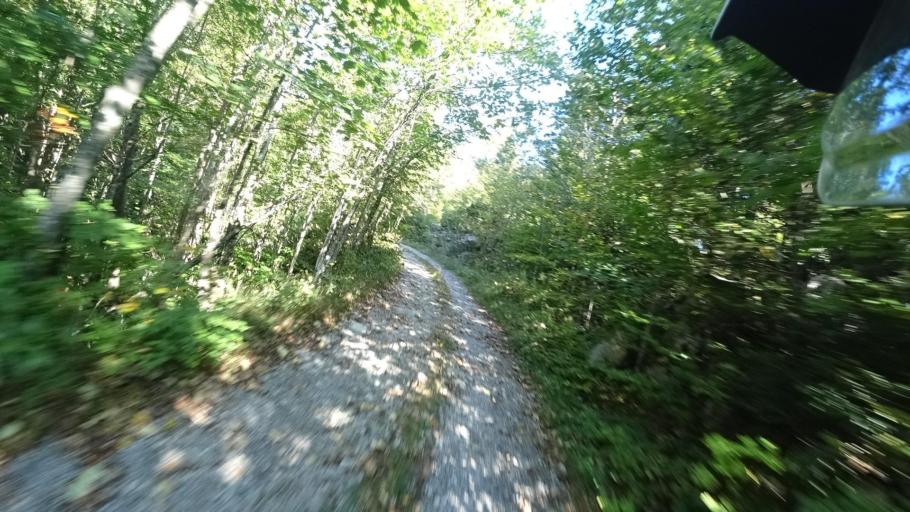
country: HR
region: Primorsko-Goranska
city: Vrbovsko
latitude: 45.2838
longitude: 15.1207
